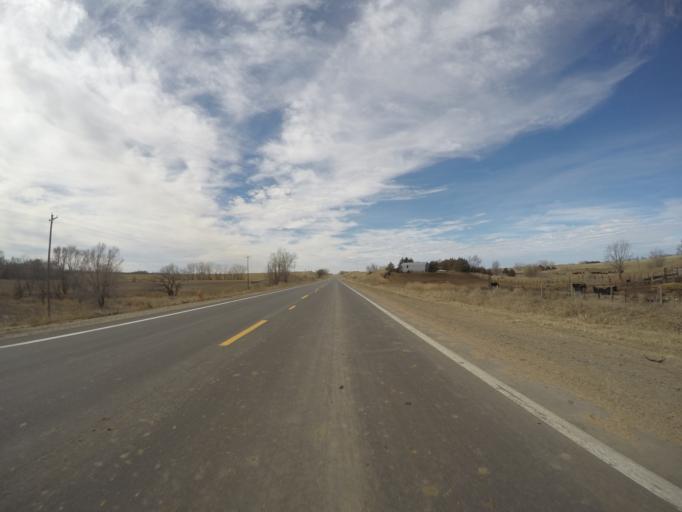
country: US
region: Nebraska
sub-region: Franklin County
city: Franklin
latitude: 40.0969
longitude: -98.7976
